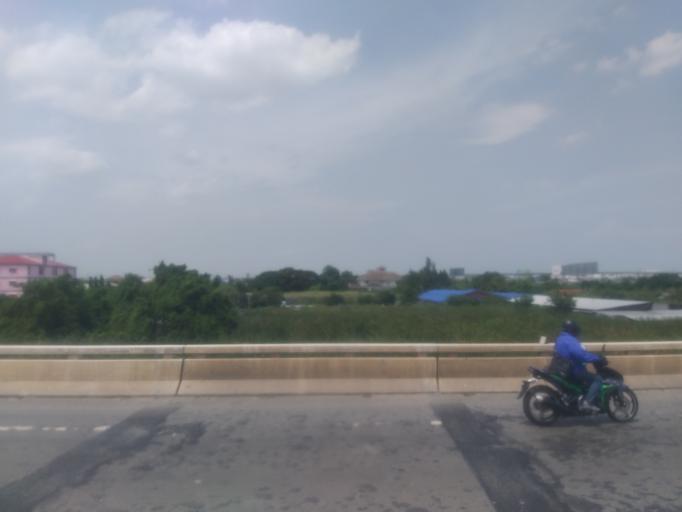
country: TH
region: Bangkok
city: Lat Krabang
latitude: 13.7203
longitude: 100.7467
